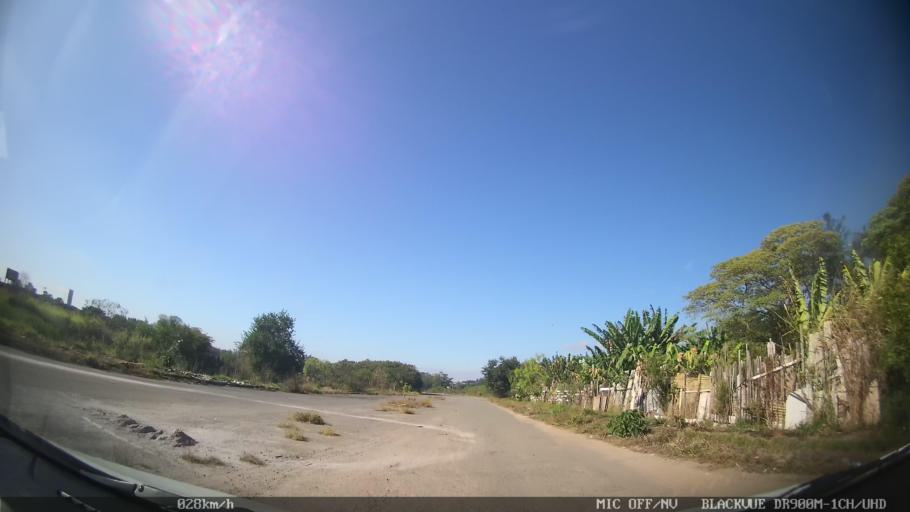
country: BR
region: Sao Paulo
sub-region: Campinas
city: Campinas
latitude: -22.9546
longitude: -47.1204
